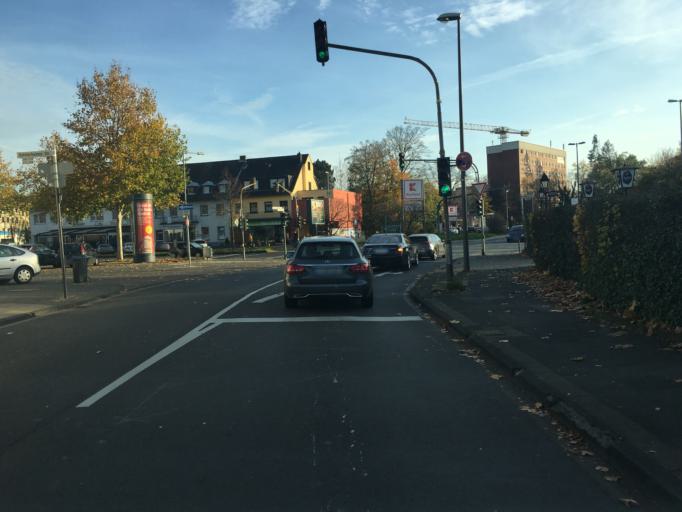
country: DE
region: North Rhine-Westphalia
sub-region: Regierungsbezirk Koln
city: Merheim
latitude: 50.9432
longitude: 7.0492
